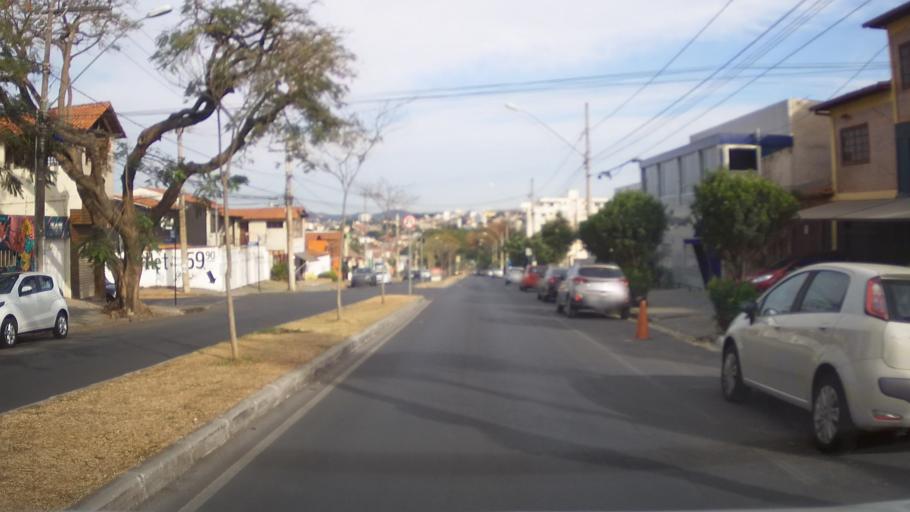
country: BR
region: Minas Gerais
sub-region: Contagem
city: Contagem
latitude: -19.8900
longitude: -44.0009
